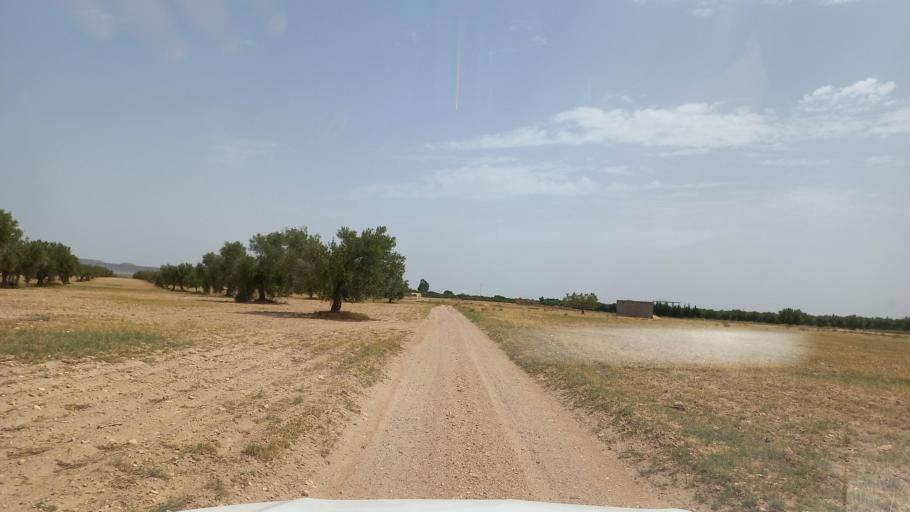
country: TN
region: Al Qasrayn
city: Kasserine
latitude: 35.2877
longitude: 9.0308
